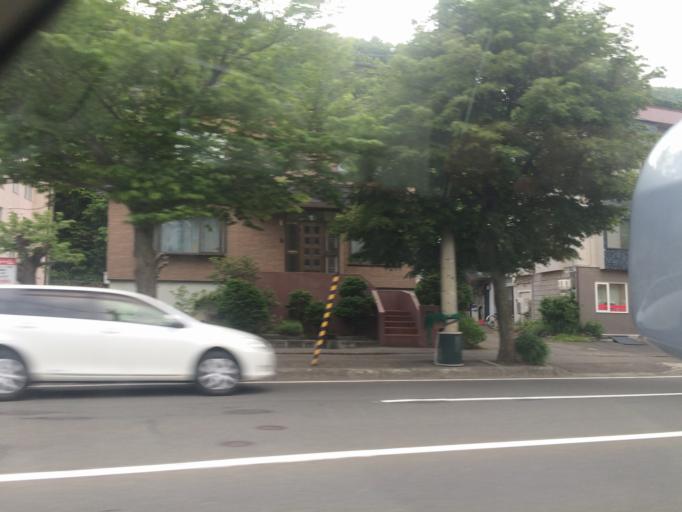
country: JP
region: Hokkaido
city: Sapporo
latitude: 43.0271
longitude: 141.3386
